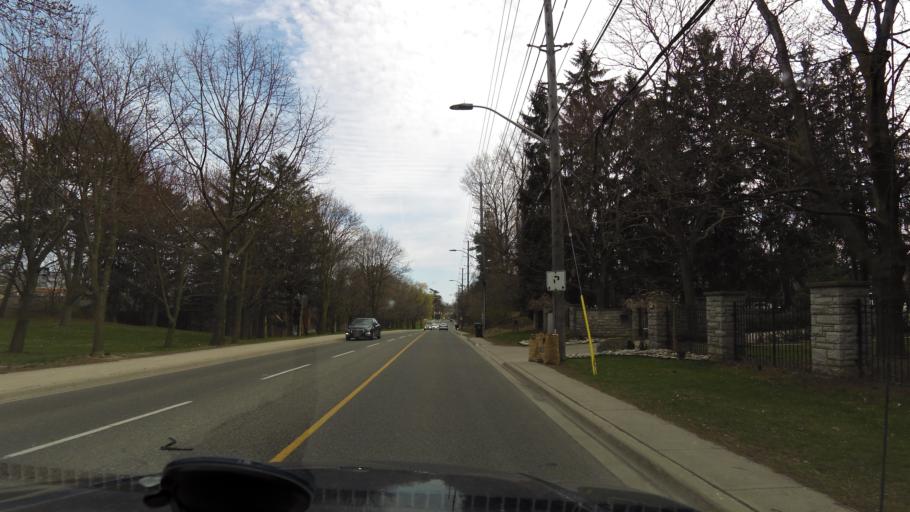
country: CA
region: Ontario
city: Mississauga
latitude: 43.5489
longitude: -79.6689
